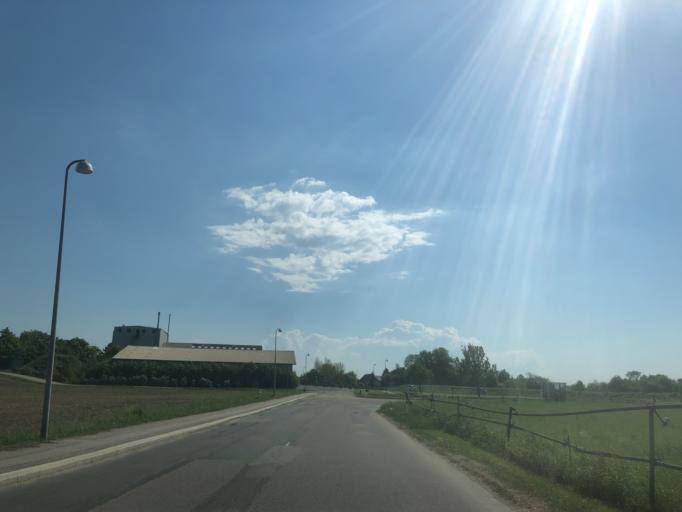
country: DK
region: Zealand
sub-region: Greve Kommune
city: Tune
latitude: 55.6176
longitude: 12.1866
